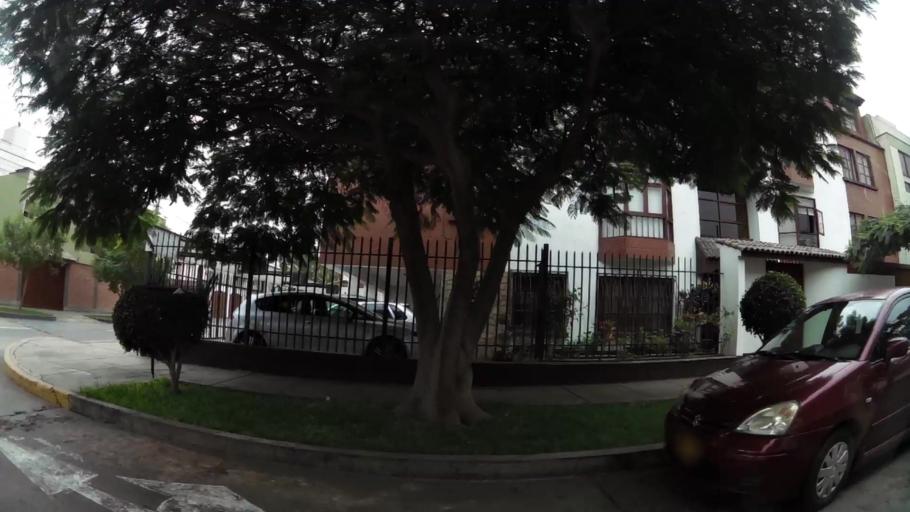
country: PE
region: Lima
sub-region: Lima
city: Surco
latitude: -12.1169
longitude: -76.9944
